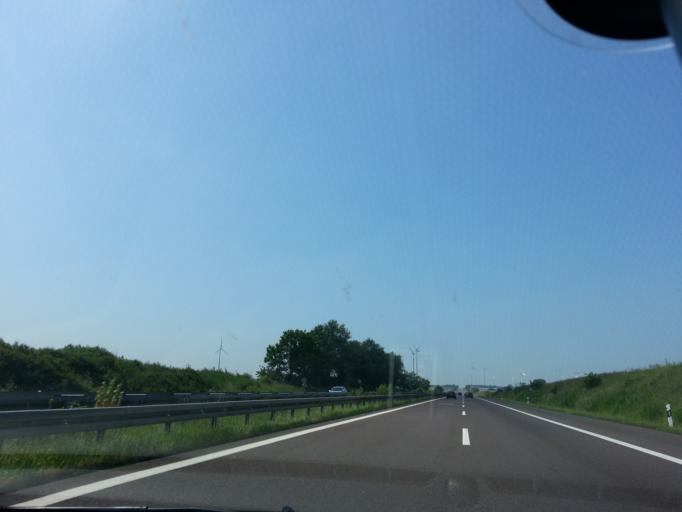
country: DE
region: Brandenburg
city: Gerdshagen
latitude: 53.2066
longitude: 12.2593
